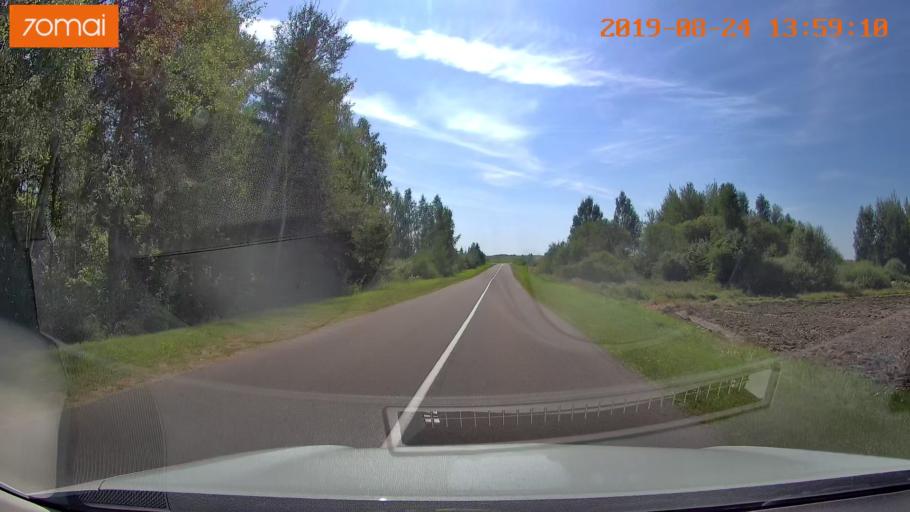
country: BY
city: Michanovichi
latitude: 53.6017
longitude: 27.6787
